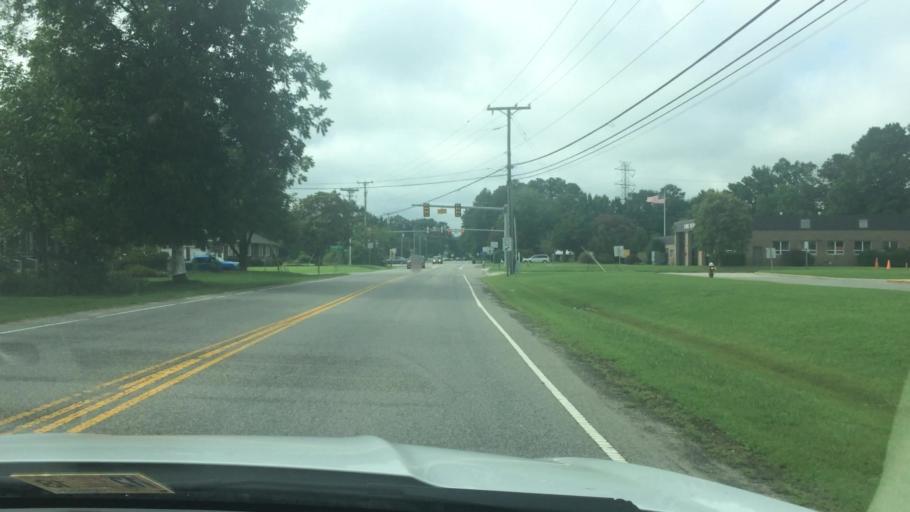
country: US
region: Virginia
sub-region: City of Poquoson
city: Poquoson
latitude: 37.1236
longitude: -76.4327
